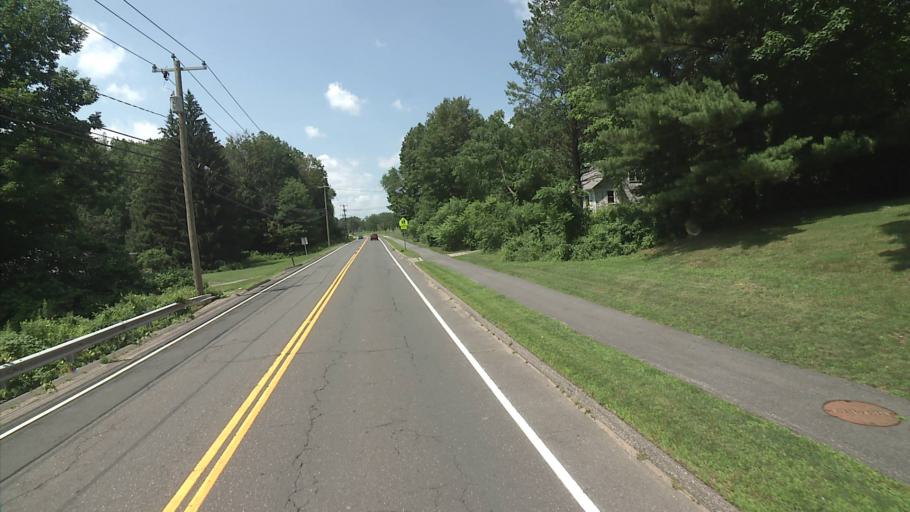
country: US
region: Connecticut
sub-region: Tolland County
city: South Coventry
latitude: 41.7780
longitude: -72.3099
